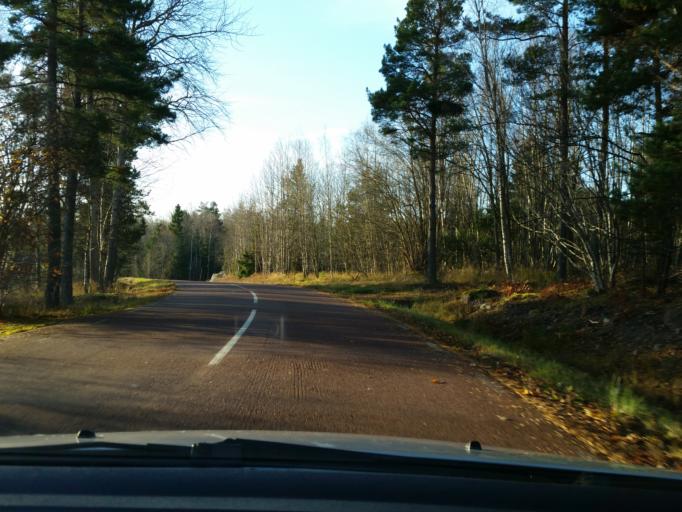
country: AX
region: Alands landsbygd
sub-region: Sund
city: Sund
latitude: 60.3073
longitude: 20.1891
